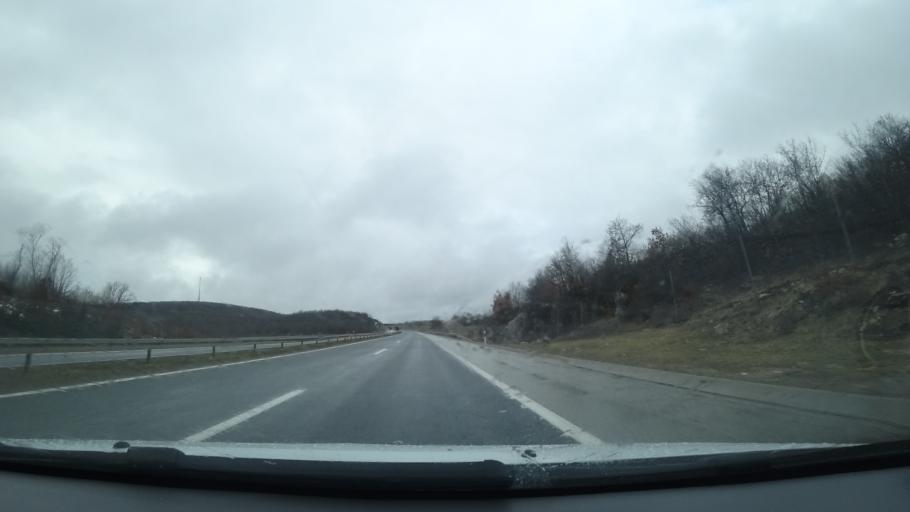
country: HR
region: Licko-Senjska
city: Gospic
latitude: 44.6931
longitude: 15.4022
